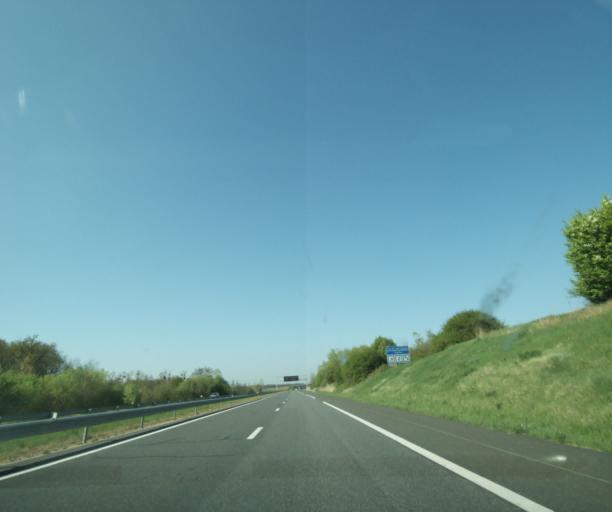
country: FR
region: Centre
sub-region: Departement du Loiret
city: Vimory
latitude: 47.9639
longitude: 2.6740
